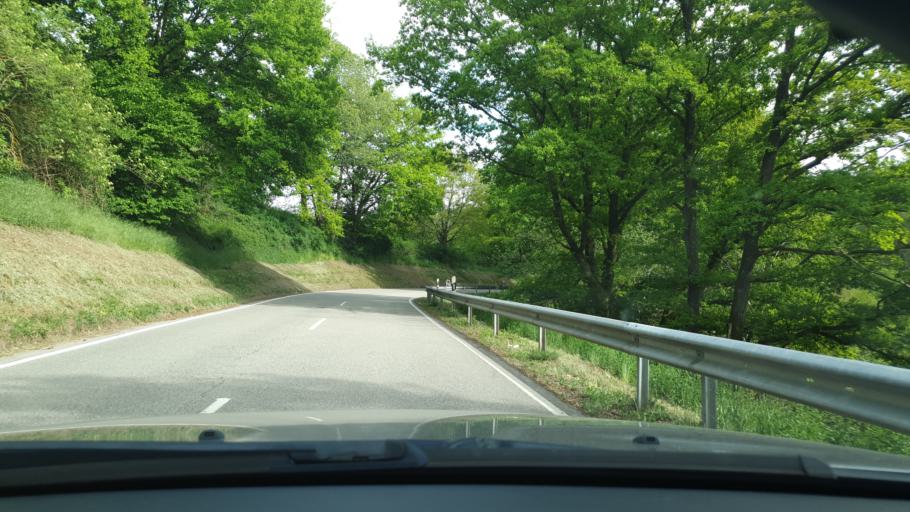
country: DE
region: Rheinland-Pfalz
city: Knopp-Labach
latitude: 49.3192
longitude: 7.5101
